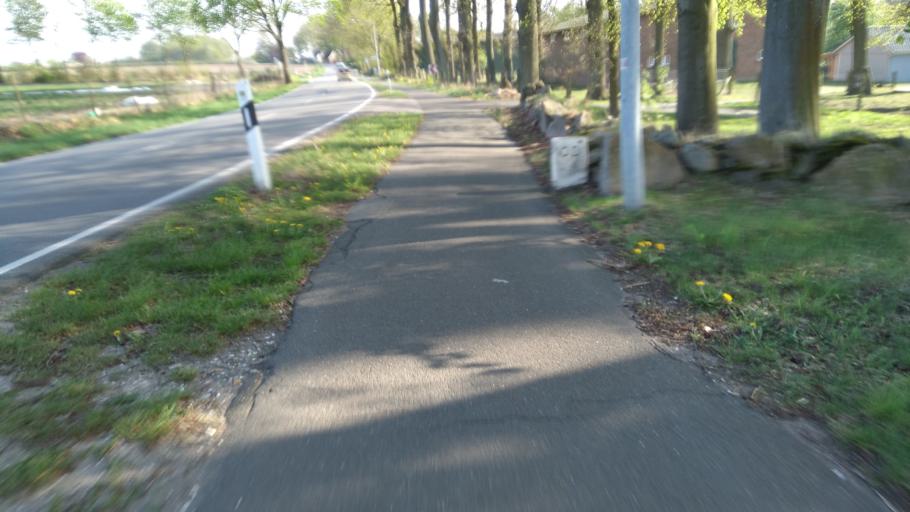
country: DE
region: Lower Saxony
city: Buxtehude
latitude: 53.4403
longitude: 9.6920
